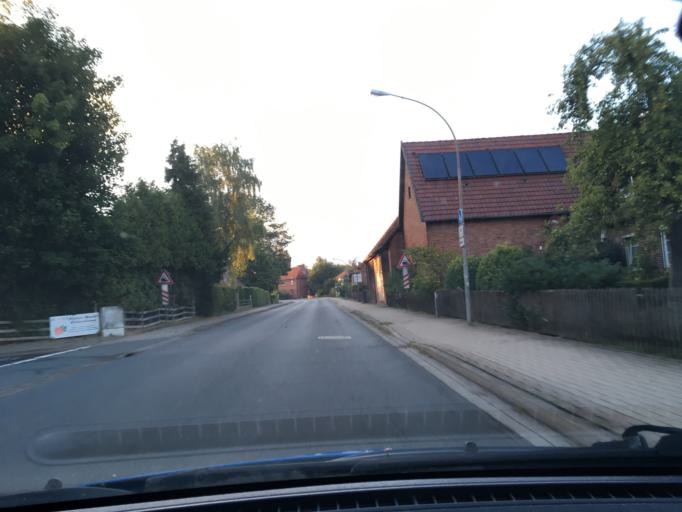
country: DE
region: Lower Saxony
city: Hermannsburg
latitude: 52.8417
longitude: 10.0854
